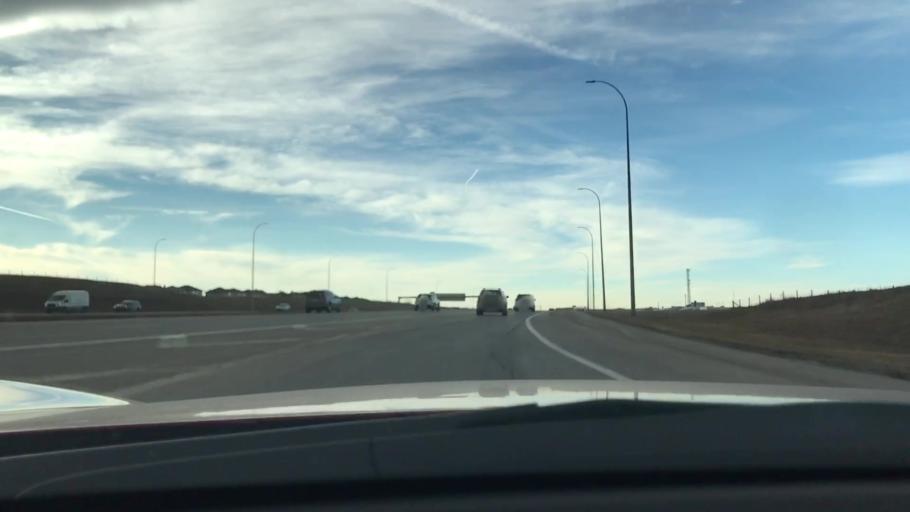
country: CA
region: Alberta
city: Calgary
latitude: 51.1520
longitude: -114.1698
